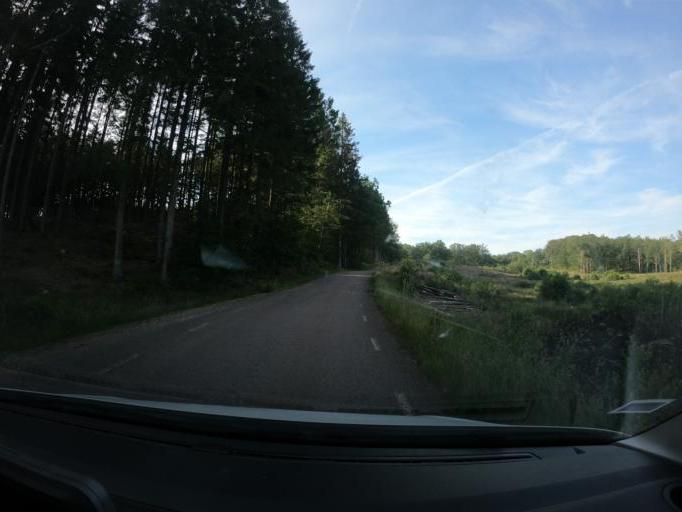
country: SE
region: Skane
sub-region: Orkelljunga Kommun
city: OErkelljunga
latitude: 56.3506
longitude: 13.1246
